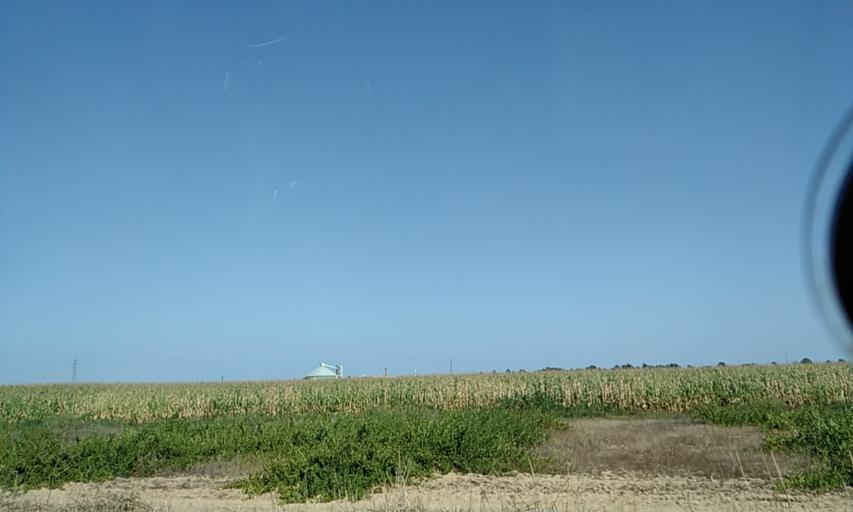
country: PT
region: Santarem
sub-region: Coruche
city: Coruche
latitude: 38.9349
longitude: -8.5167
